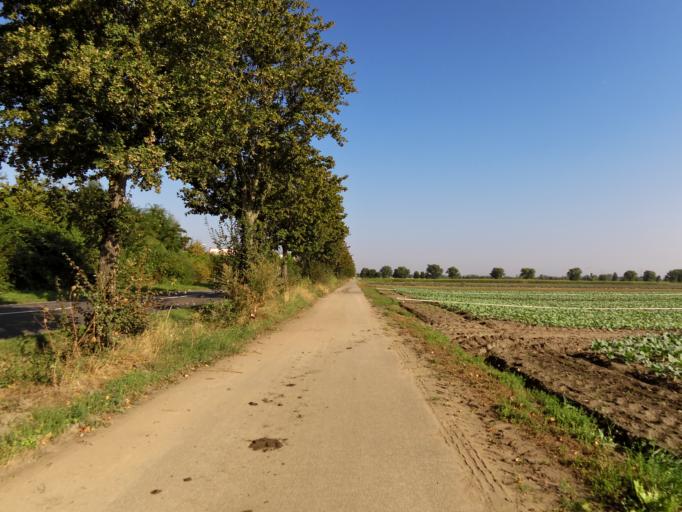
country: DE
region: Rheinland-Pfalz
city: Maxdorf
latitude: 49.4893
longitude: 8.2952
